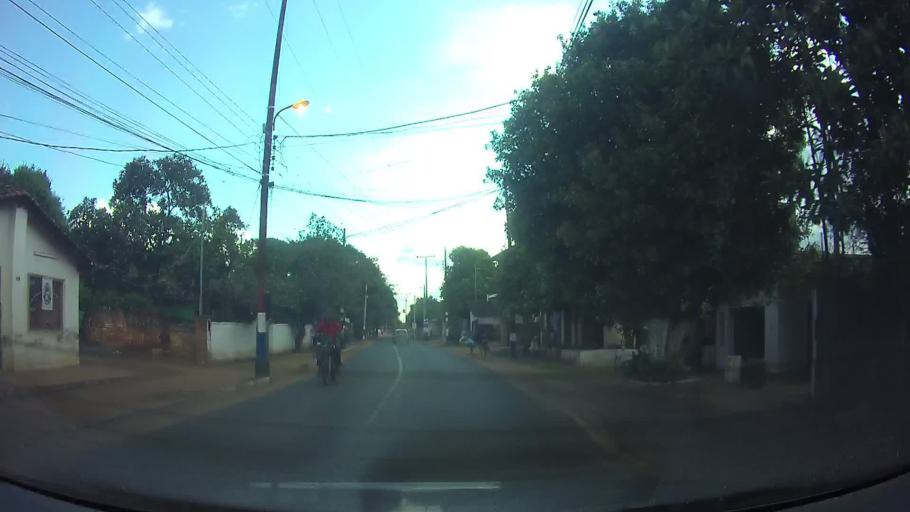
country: PY
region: Central
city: Aregua
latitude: -25.2855
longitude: -57.4380
